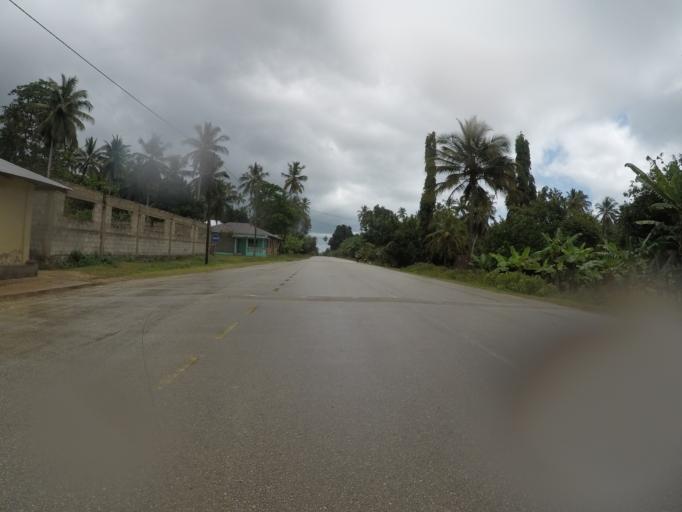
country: TZ
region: Zanzibar North
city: Mkokotoni
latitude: -5.9710
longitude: 39.1966
